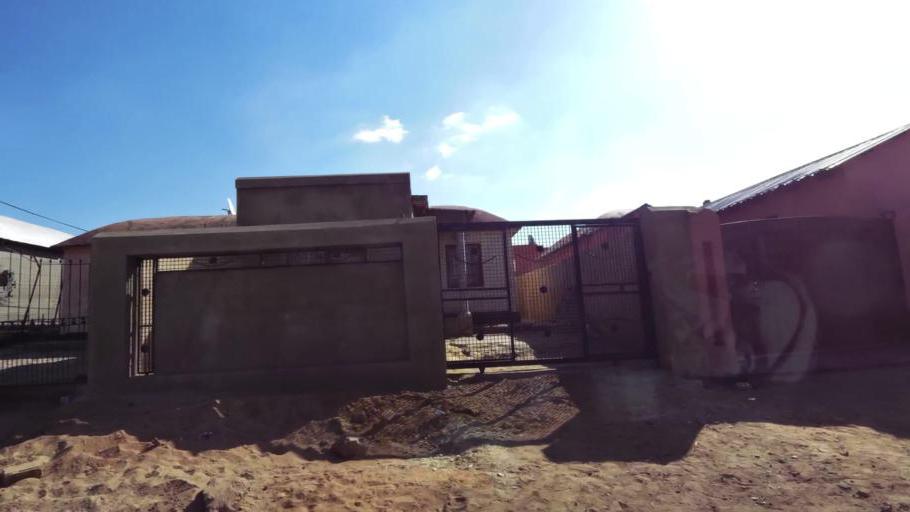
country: ZA
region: Gauteng
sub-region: City of Johannesburg Metropolitan Municipality
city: Soweto
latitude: -26.2251
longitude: 27.9208
